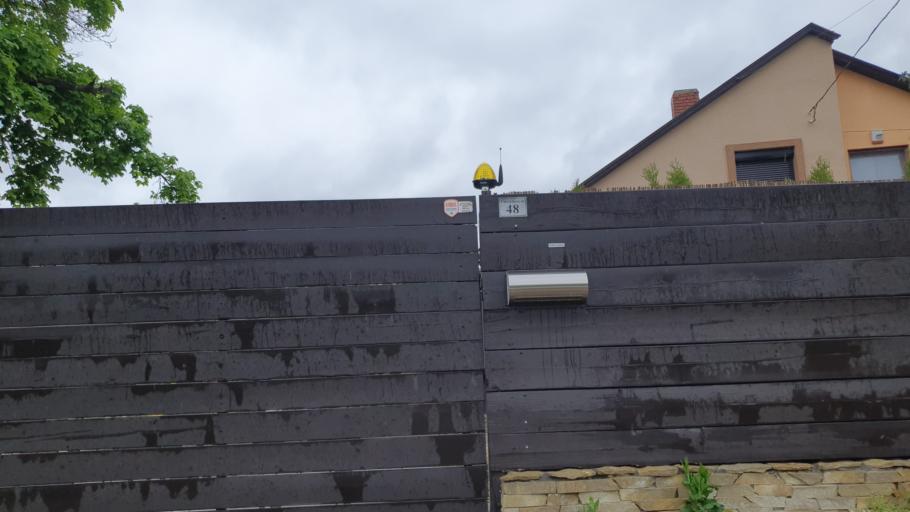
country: HU
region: Komarom-Esztergom
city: Esztergom
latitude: 47.7942
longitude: 18.8044
